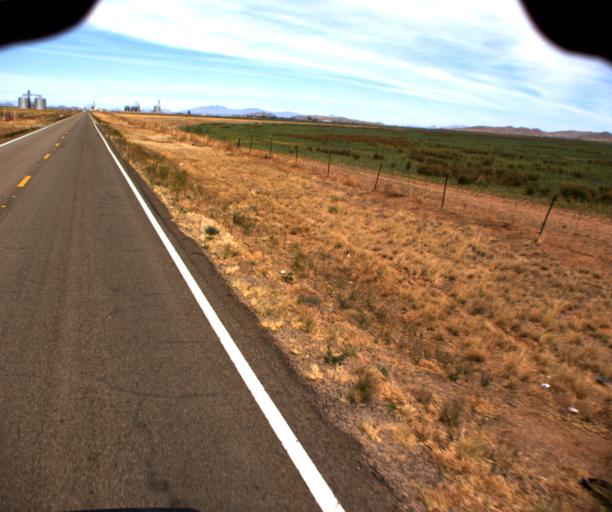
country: US
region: Arizona
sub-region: Cochise County
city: Tombstone
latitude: 31.7466
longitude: -109.6885
